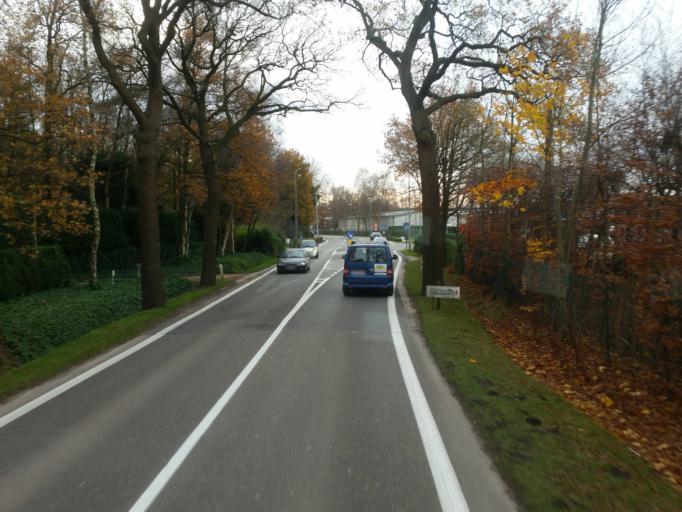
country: BE
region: Flanders
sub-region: Provincie Antwerpen
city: Kalmthout
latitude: 51.3630
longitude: 4.5064
